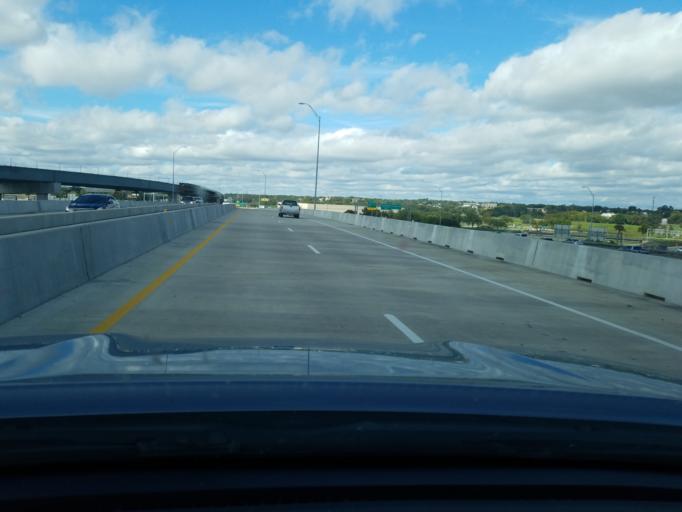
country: US
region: Texas
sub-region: Tarrant County
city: Fort Worth
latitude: 32.7648
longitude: -97.3180
